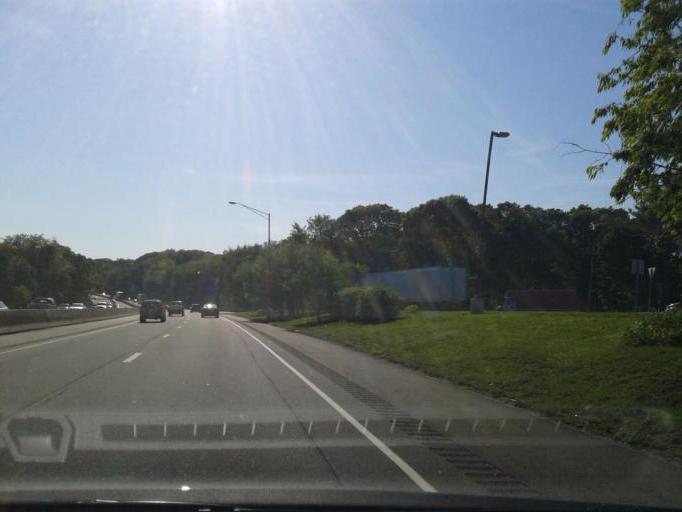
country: US
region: Connecticut
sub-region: New Haven County
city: Madison
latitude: 41.2914
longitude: -72.5812
